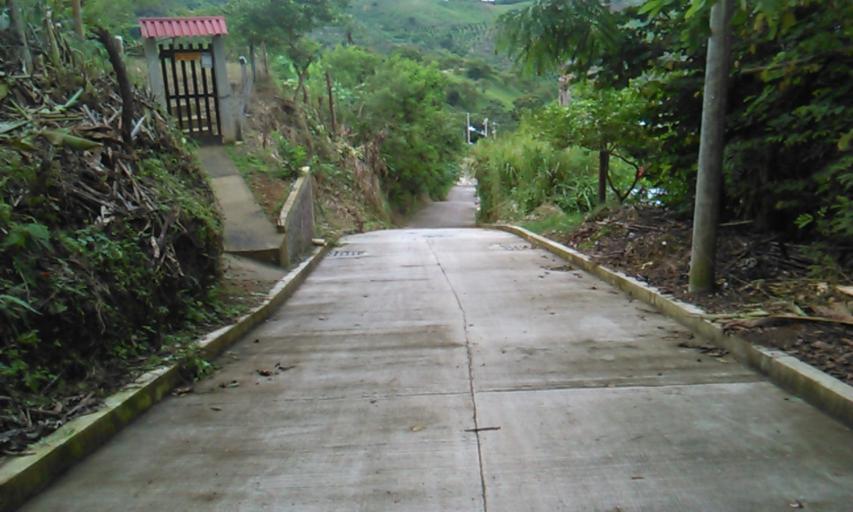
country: CO
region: Quindio
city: Cordoba
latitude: 4.3891
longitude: -75.6857
